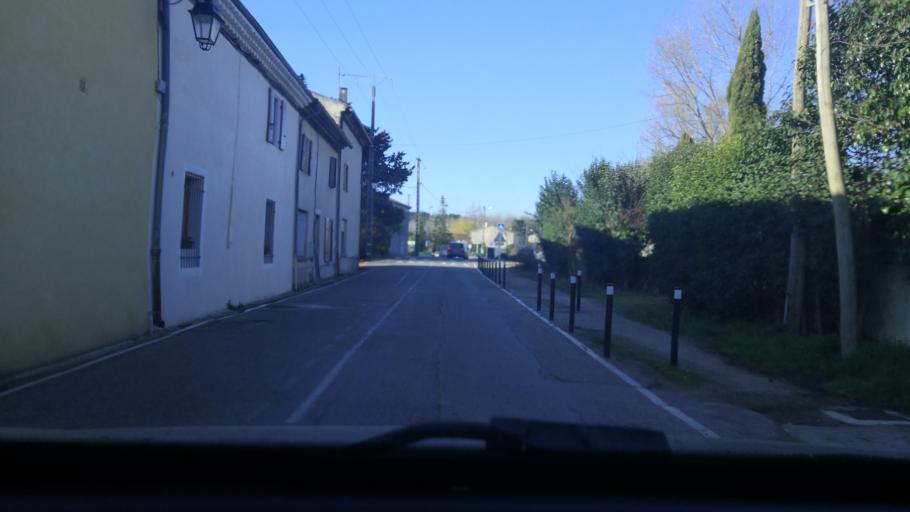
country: FR
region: Rhone-Alpes
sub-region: Departement de la Drome
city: Saint-Marcel-les-Sauzet
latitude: 44.5955
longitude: 4.8040
